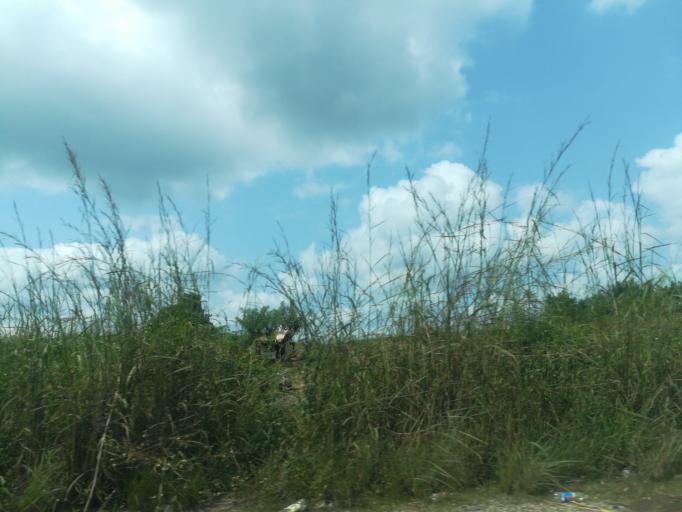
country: NG
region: Oyo
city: Moniya
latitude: 7.5900
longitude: 3.9133
